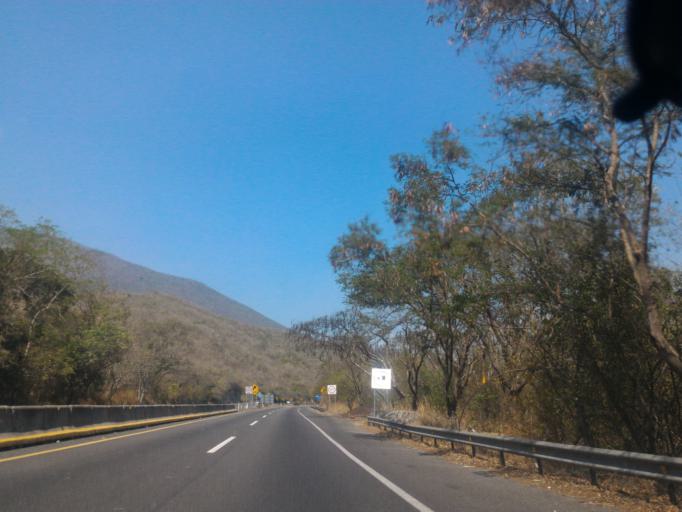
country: MX
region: Colima
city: Ixtlahuacan
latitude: 19.0289
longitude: -103.7945
